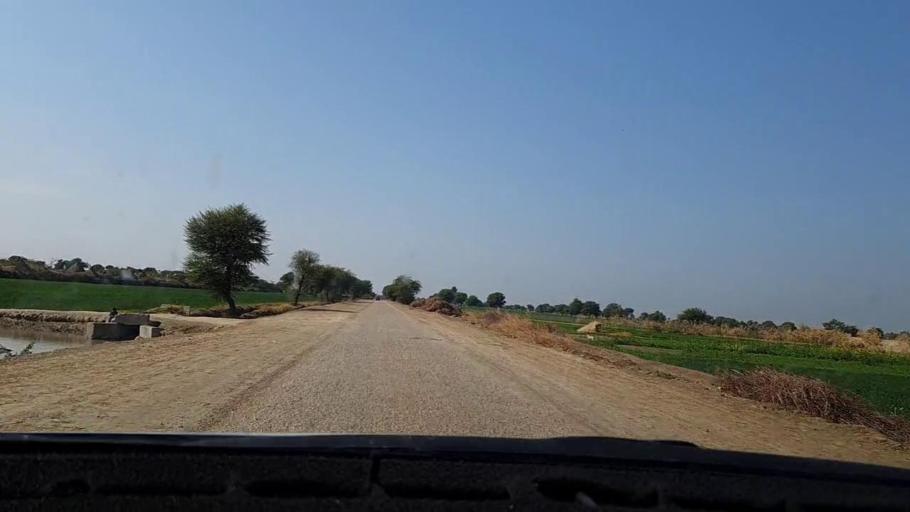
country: PK
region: Sindh
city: Tando Mittha Khan
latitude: 25.8075
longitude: 69.3260
